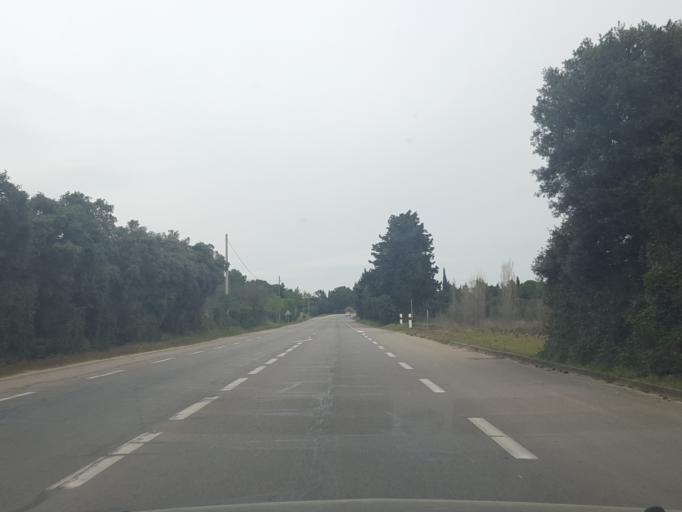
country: FR
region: Provence-Alpes-Cote d'Azur
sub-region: Departement du Vaucluse
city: Saint-Saturnin-les-Avignon
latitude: 43.9538
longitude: 4.9121
